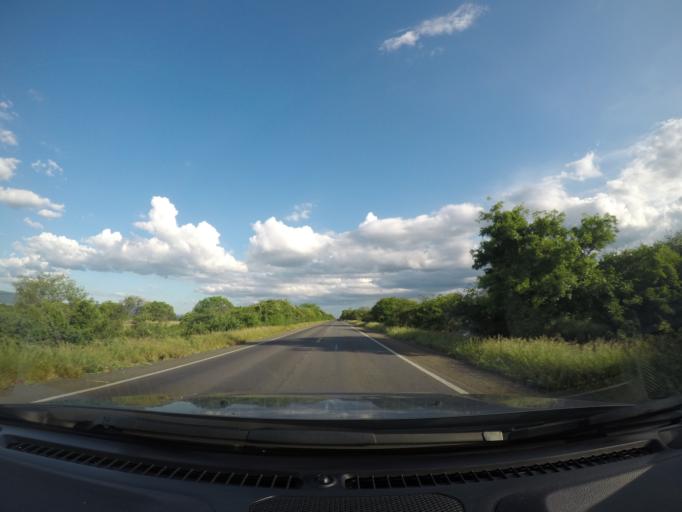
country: BR
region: Bahia
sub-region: Oliveira Dos Brejinhos
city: Beira Rio
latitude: -12.2221
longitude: -42.7903
